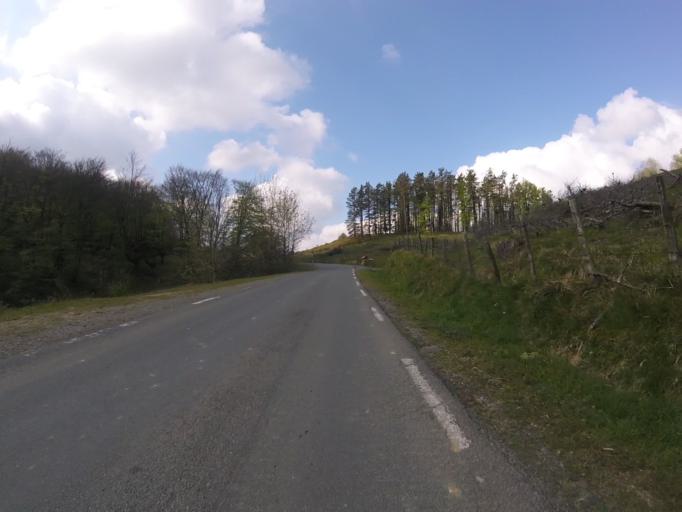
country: ES
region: Basque Country
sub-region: Provincia de Guipuzcoa
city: Azkoitia
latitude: 43.2102
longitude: -2.3209
